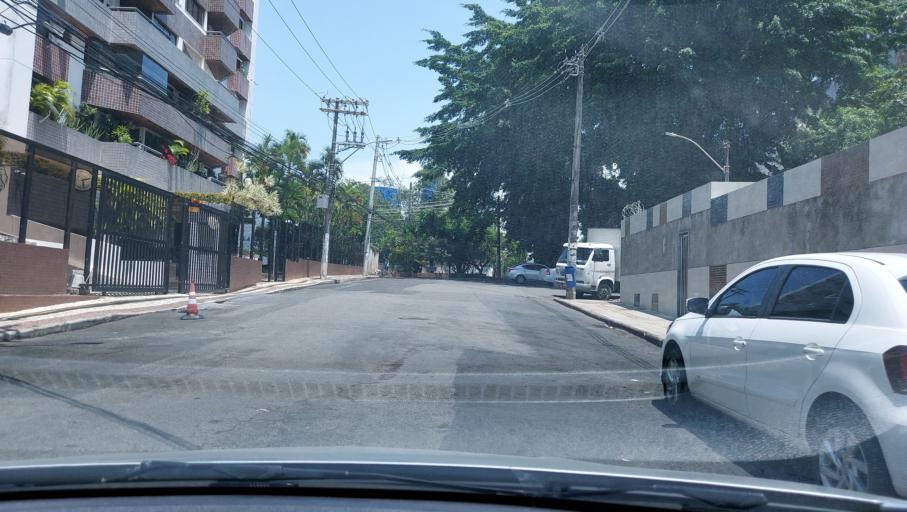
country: BR
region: Bahia
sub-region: Salvador
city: Salvador
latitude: -12.9846
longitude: -38.4630
